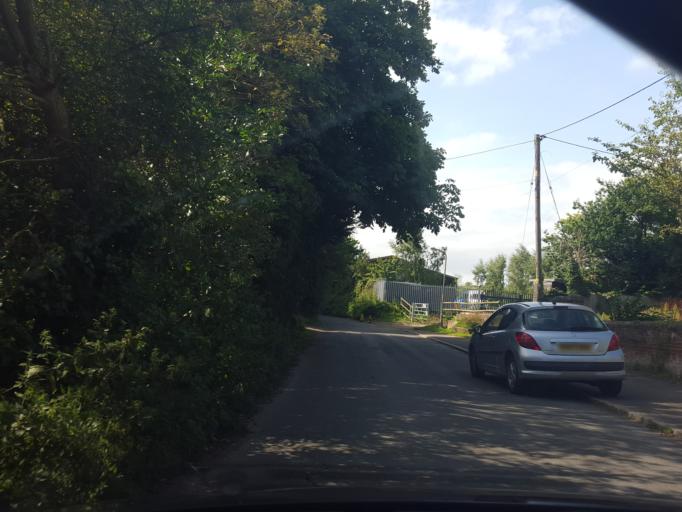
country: GB
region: England
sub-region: Suffolk
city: Shotley Gate
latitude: 51.9267
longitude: 1.2093
